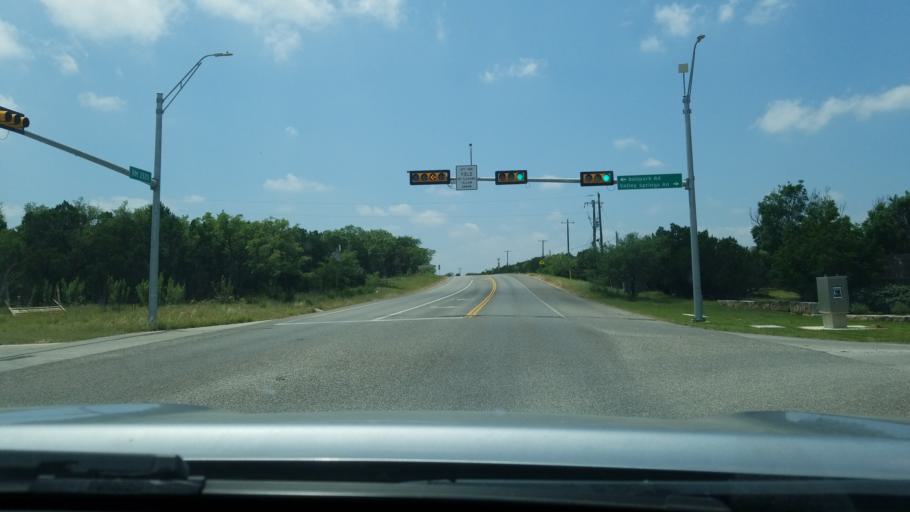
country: US
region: Texas
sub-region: Hays County
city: Woodcreek
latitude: 30.0197
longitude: -98.1382
